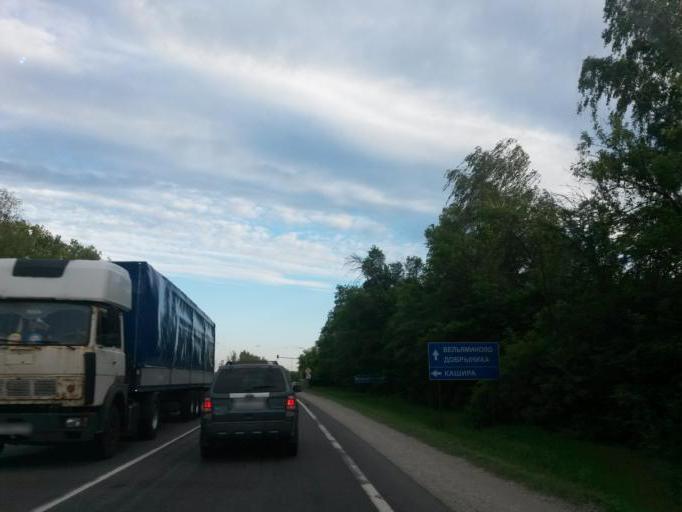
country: RU
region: Moskovskaya
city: Barybino
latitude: 55.2058
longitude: 37.8687
